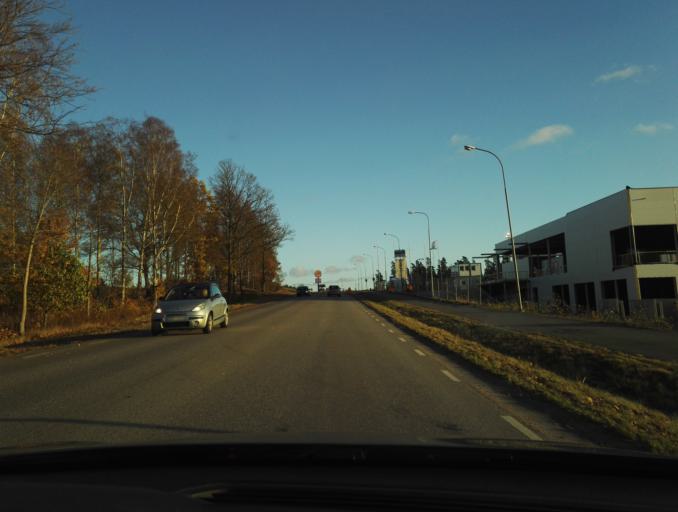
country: SE
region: Kronoberg
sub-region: Vaxjo Kommun
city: Vaexjoe
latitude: 56.8808
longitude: 14.7605
